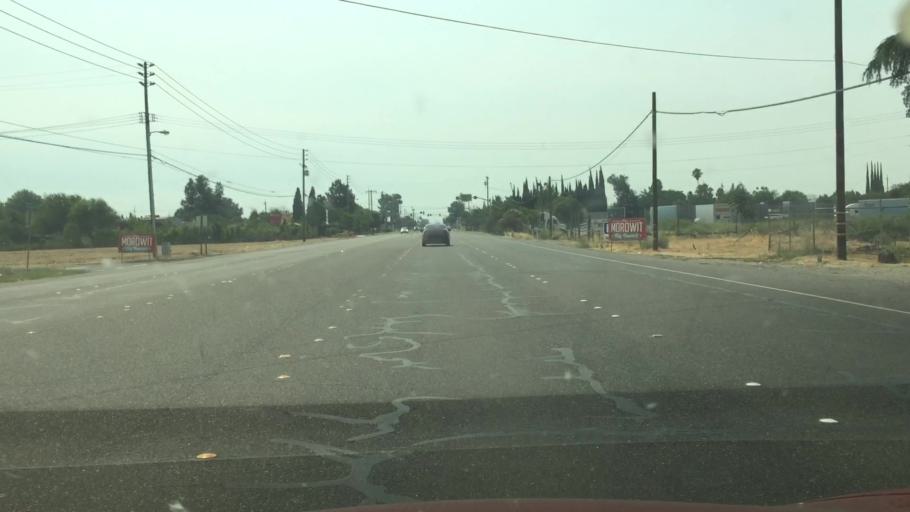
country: US
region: California
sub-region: San Joaquin County
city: Manteca
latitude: 37.7974
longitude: -121.2476
